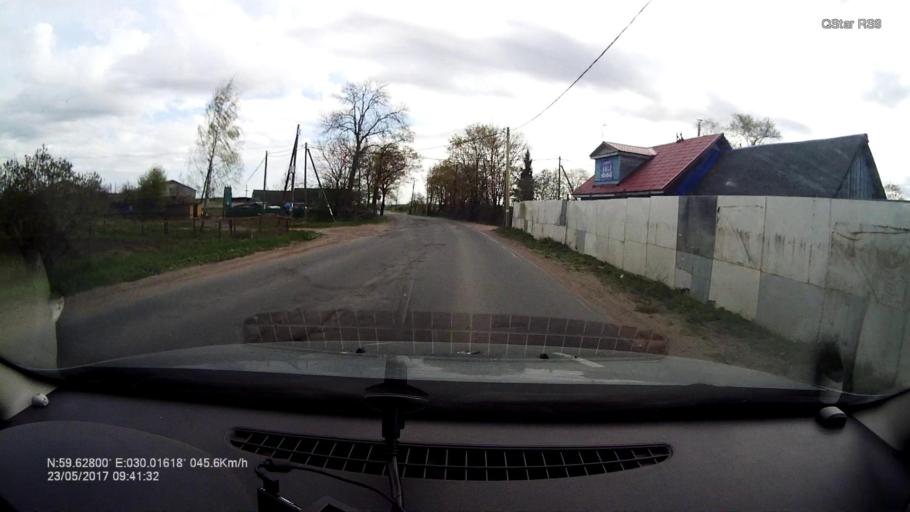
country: RU
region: Leningrad
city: Mariyenburg
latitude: 59.6281
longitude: 30.0165
